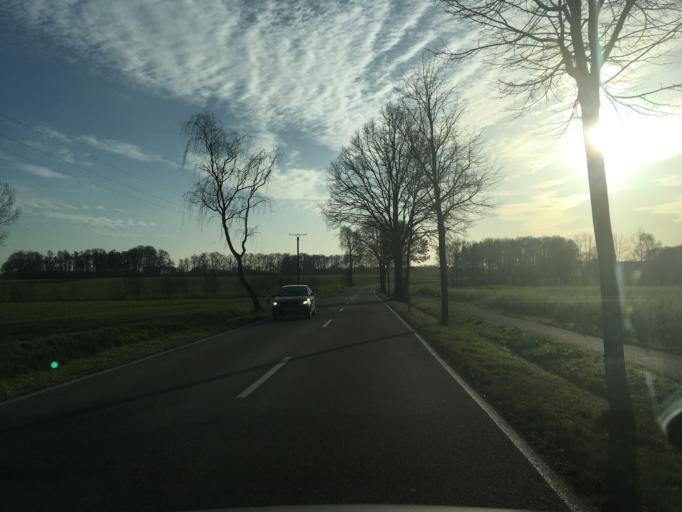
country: DE
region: North Rhine-Westphalia
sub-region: Regierungsbezirk Munster
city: Gescher
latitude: 51.9526
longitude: 7.0582
